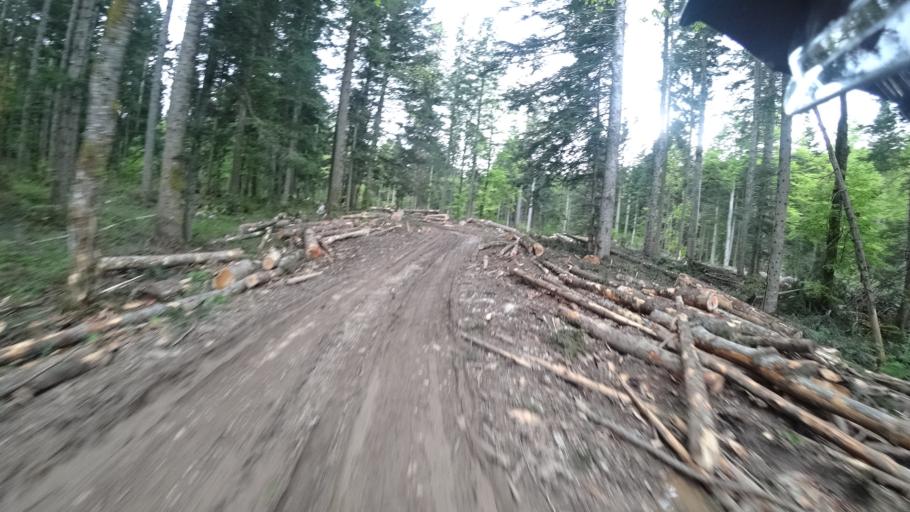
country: HR
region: Karlovacka
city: Plaski
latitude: 44.9504
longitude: 15.4150
